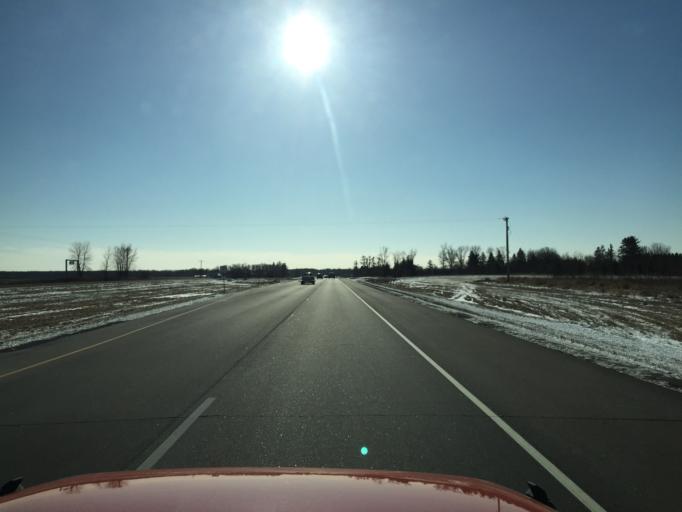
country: US
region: Minnesota
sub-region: Mille Lacs County
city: Milaca
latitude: 45.8420
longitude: -93.6619
